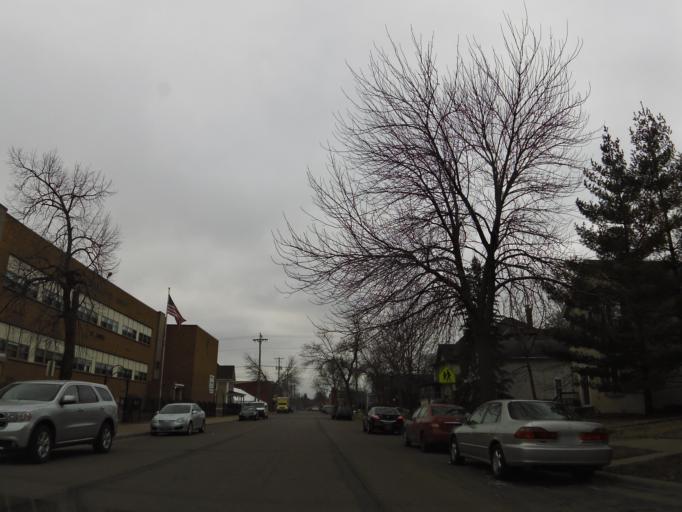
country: US
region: Minnesota
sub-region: Dakota County
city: West Saint Paul
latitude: 44.9285
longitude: -93.1282
